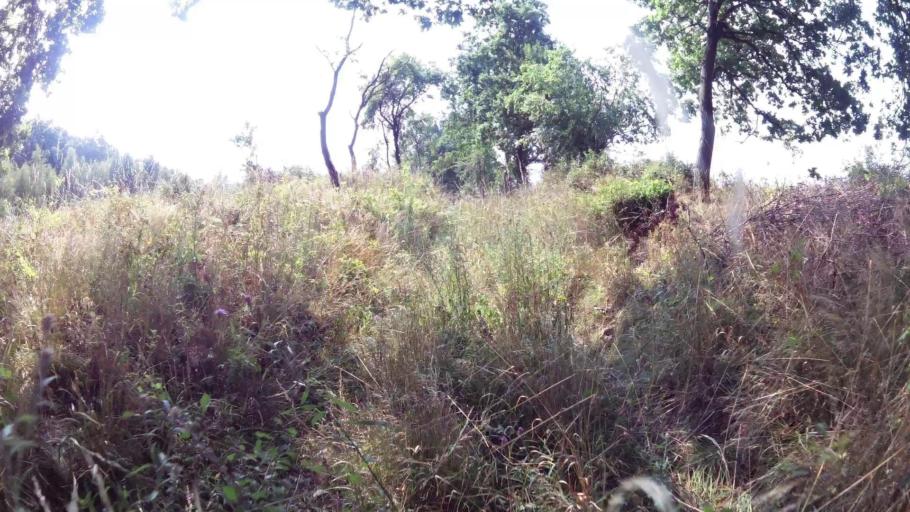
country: PL
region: West Pomeranian Voivodeship
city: Trzcinsko Zdroj
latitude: 52.9295
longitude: 14.5580
